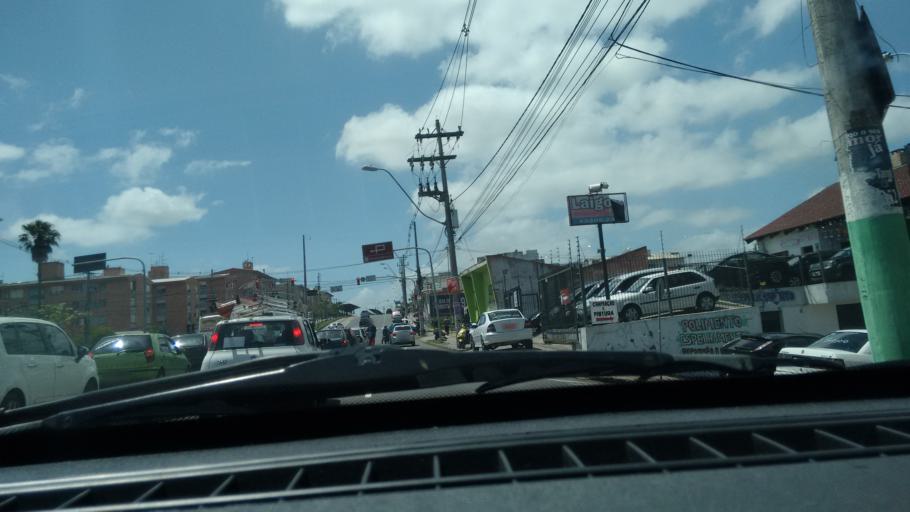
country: BR
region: Rio Grande do Sul
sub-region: Cachoeirinha
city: Cachoeirinha
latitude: -30.0150
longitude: -51.1201
